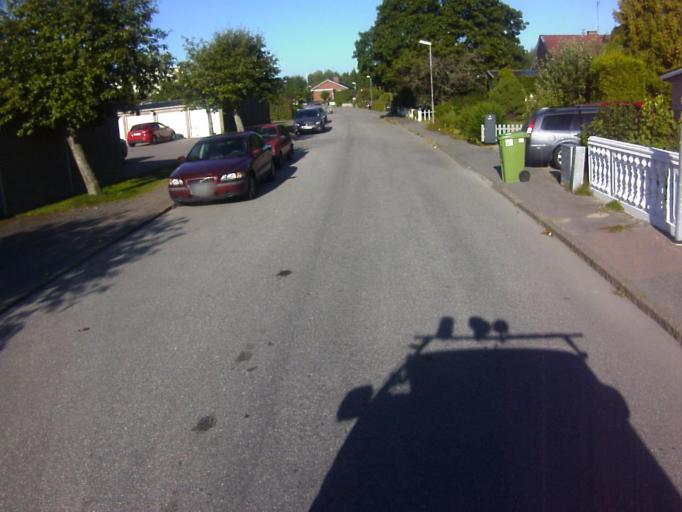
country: SE
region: Soedermanland
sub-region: Eskilstuna Kommun
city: Eskilstuna
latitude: 59.3838
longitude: 16.5312
